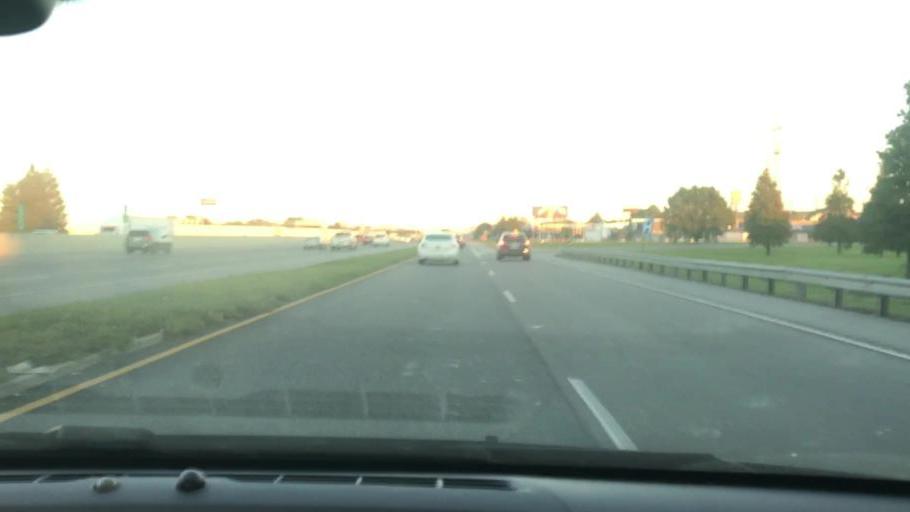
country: US
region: Louisiana
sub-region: Jefferson Parish
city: Metairie Terrace
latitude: 29.9988
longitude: -90.1839
